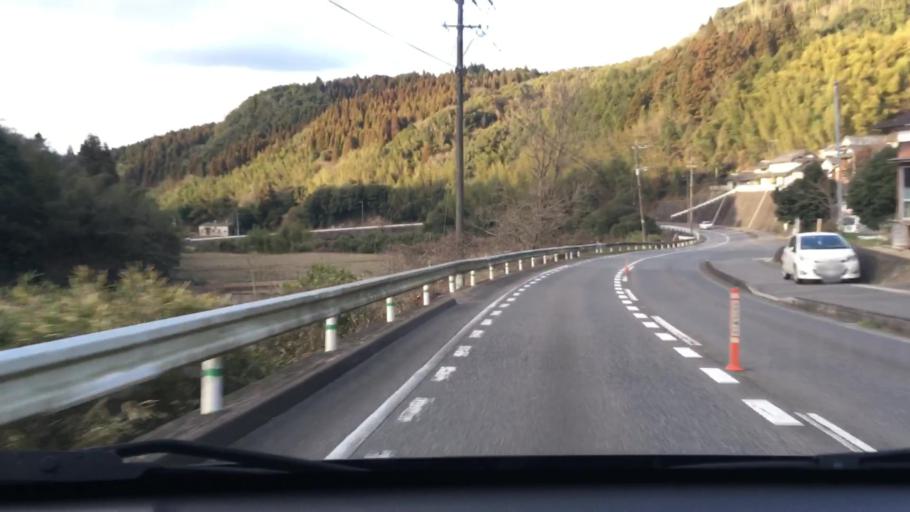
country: JP
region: Oita
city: Hiji
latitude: 33.4183
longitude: 131.4191
